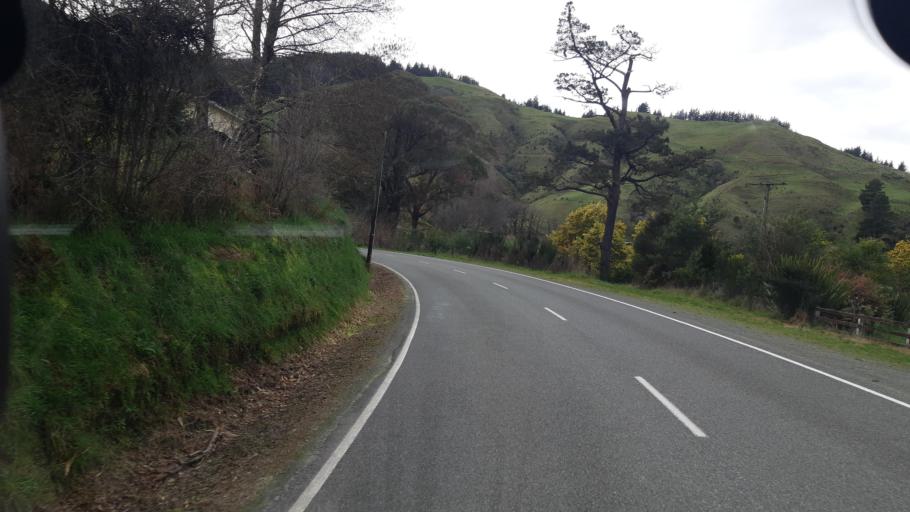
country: NZ
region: Tasman
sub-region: Tasman District
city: Motueka
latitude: -41.2689
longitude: 172.8350
